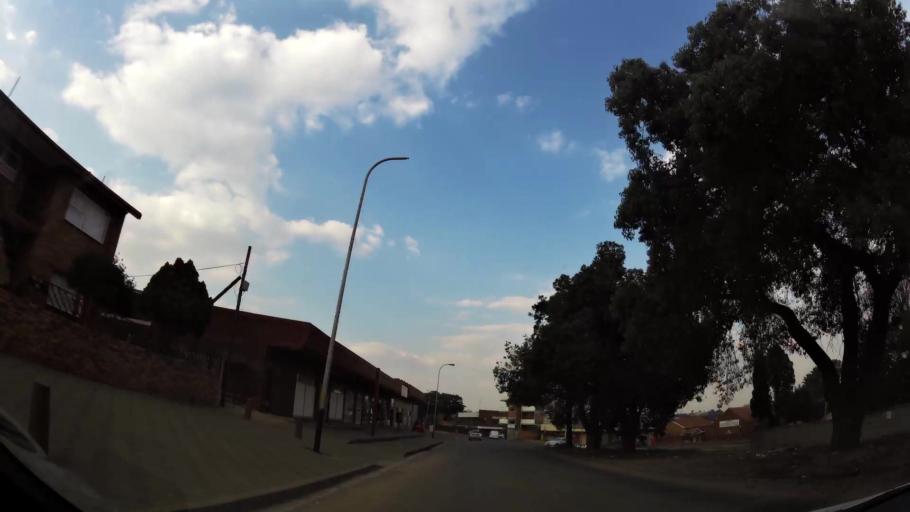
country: ZA
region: Gauteng
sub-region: Ekurhuleni Metropolitan Municipality
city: Germiston
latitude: -26.2458
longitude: 28.1989
